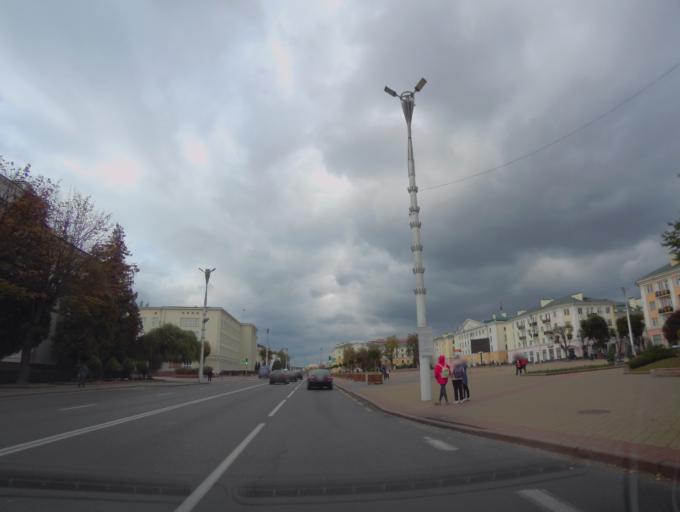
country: BY
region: Brest
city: Brest
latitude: 52.0929
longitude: 23.6855
